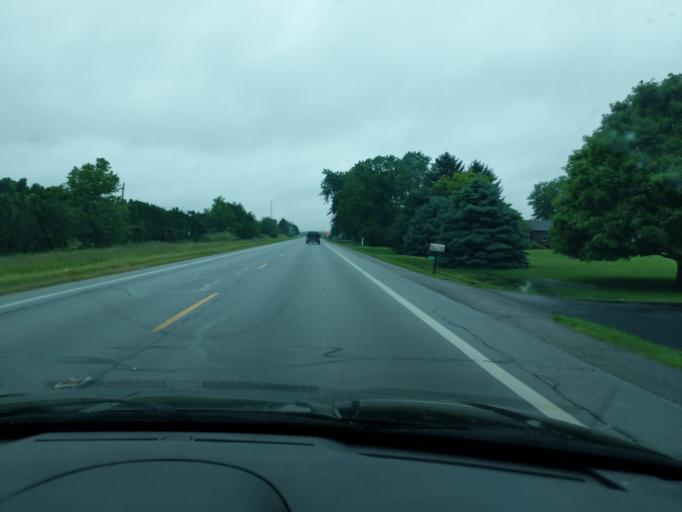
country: US
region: Ohio
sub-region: Logan County
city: West Liberty
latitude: 40.2308
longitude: -83.7520
